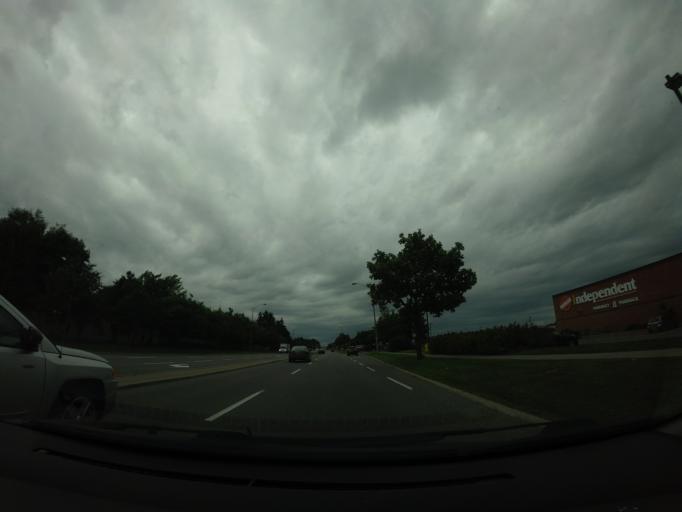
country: CA
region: Quebec
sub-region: Outaouais
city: Gatineau
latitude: 45.4593
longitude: -75.5251
